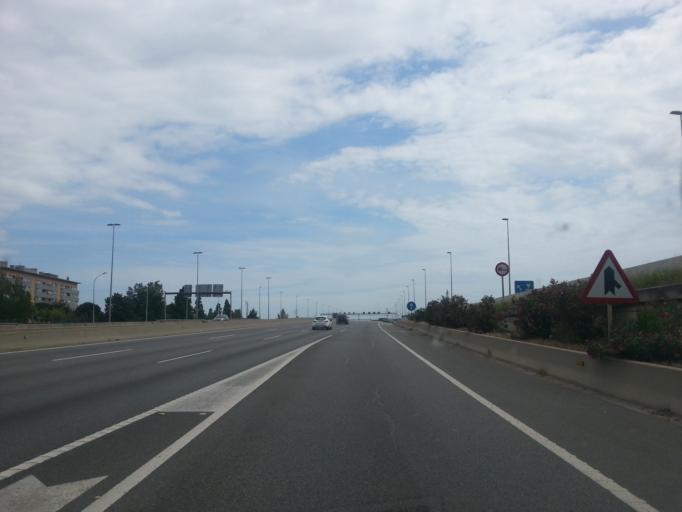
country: ES
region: Catalonia
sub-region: Provincia de Barcelona
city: Molins de Rei
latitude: 41.4082
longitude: 2.0148
